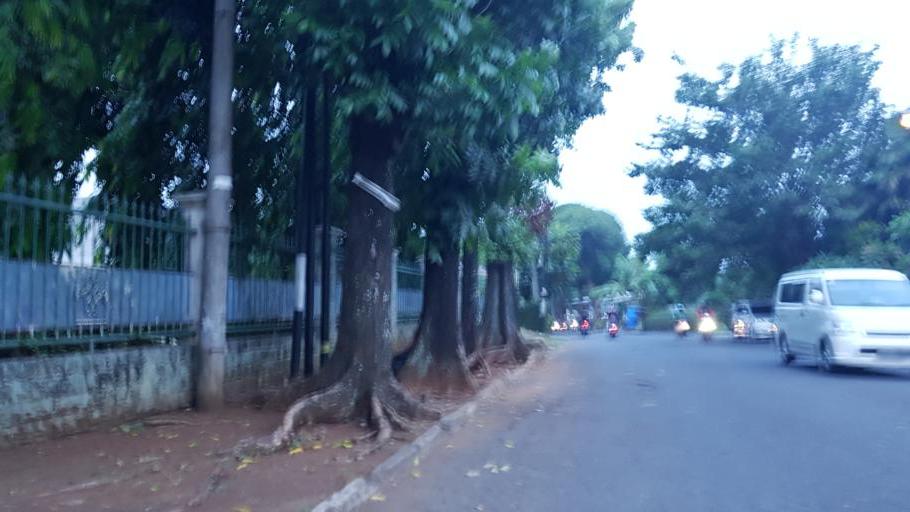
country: ID
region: West Java
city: Pamulang
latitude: -6.3188
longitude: 106.7838
